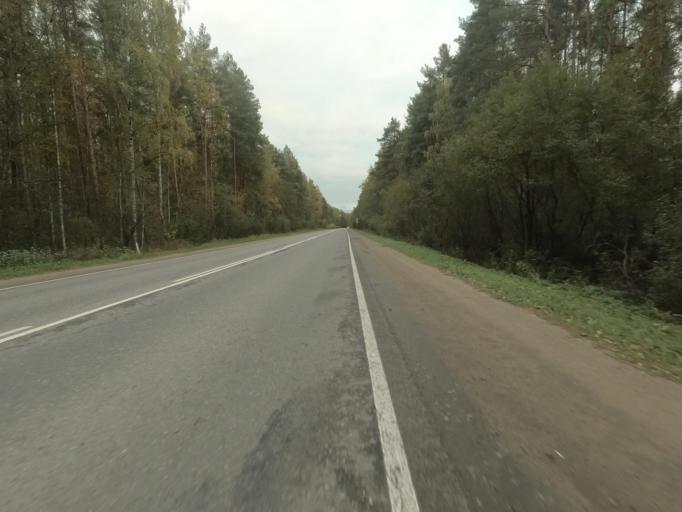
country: RU
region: Leningrad
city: Pavlovo
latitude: 59.8077
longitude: 30.9304
